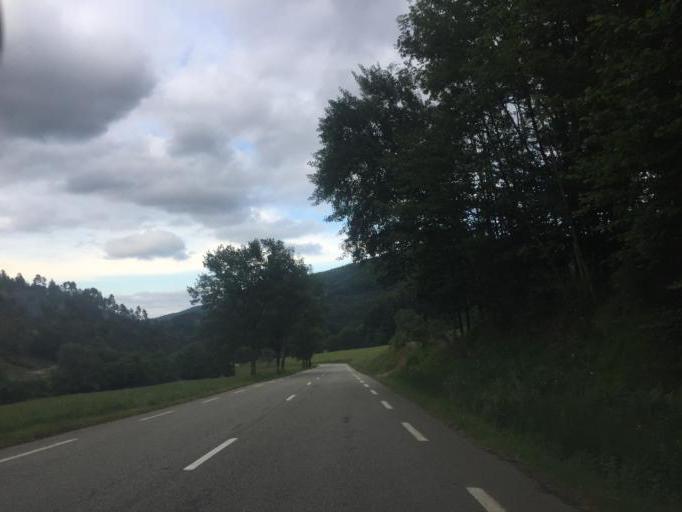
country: FR
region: Rhone-Alpes
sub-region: Departement de l'Ardeche
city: Privas
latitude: 44.7713
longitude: 4.5989
